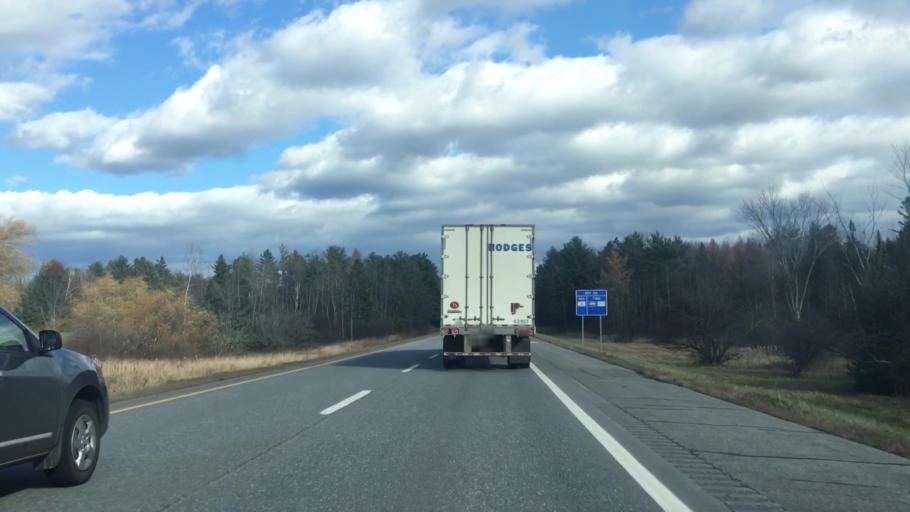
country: US
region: Maine
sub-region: Kennebec County
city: Benton
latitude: 44.6202
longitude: -69.5525
